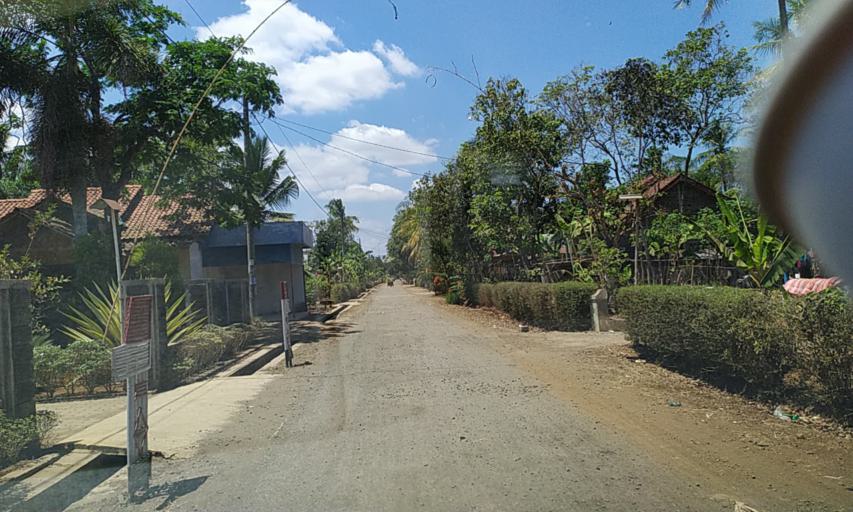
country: ID
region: Central Java
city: Kroya
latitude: -7.6489
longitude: 109.2424
